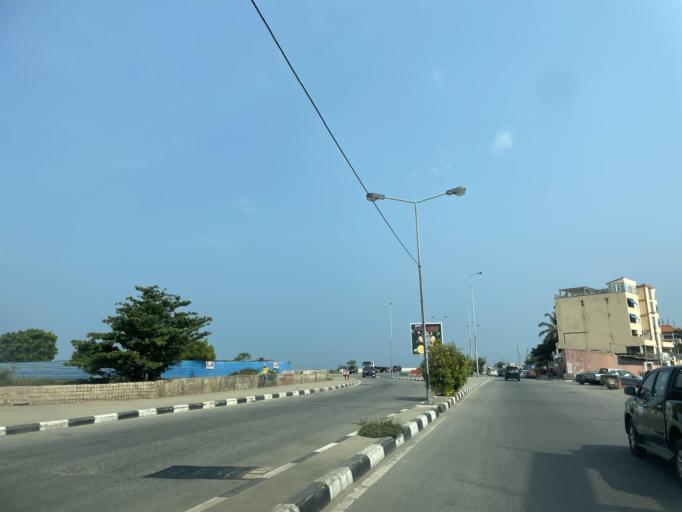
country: AO
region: Luanda
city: Luanda
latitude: -8.8298
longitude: 13.2147
